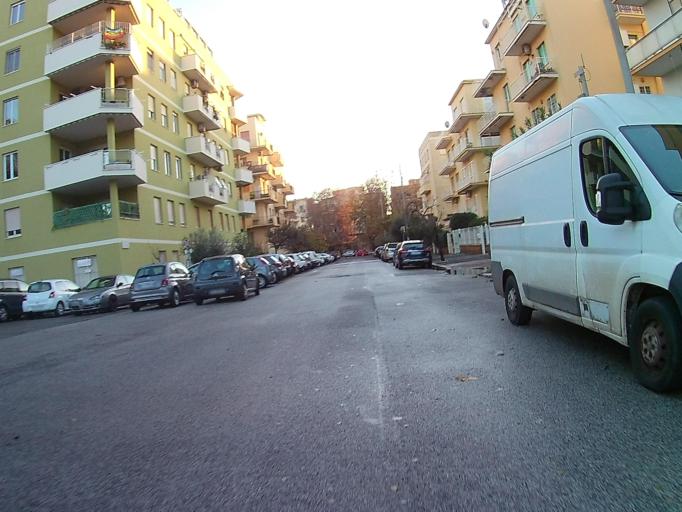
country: IT
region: Latium
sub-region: Citta metropolitana di Roma Capitale
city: Lido di Ostia
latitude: 41.7276
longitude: 12.2899
